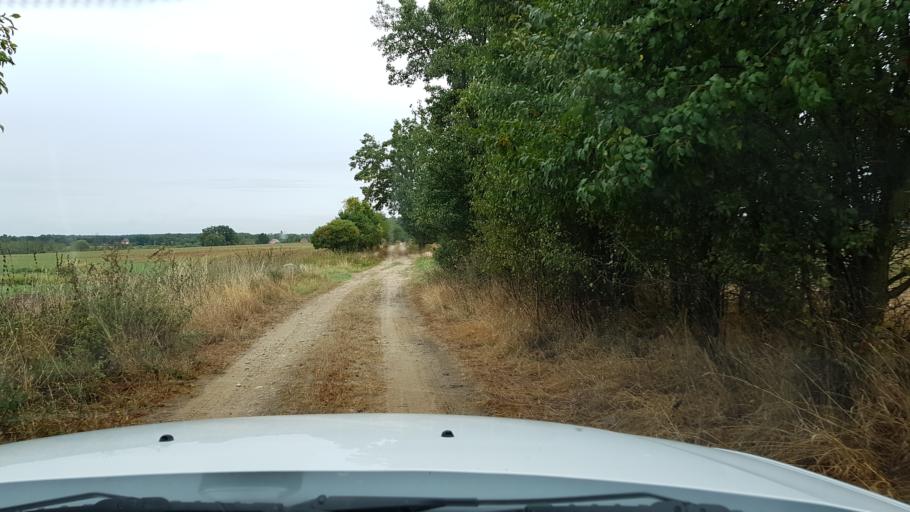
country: PL
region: West Pomeranian Voivodeship
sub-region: Powiat gryfinski
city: Chojna
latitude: 52.9017
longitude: 14.4466
